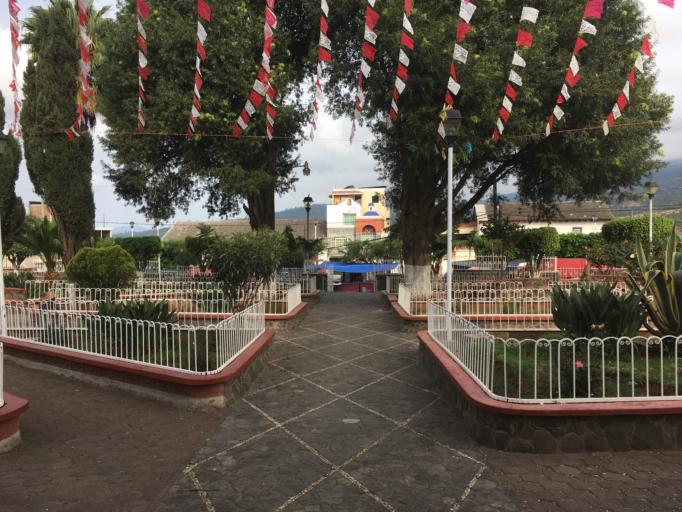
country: MX
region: Michoacan
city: Tingambato
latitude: 19.5015
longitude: -101.8538
